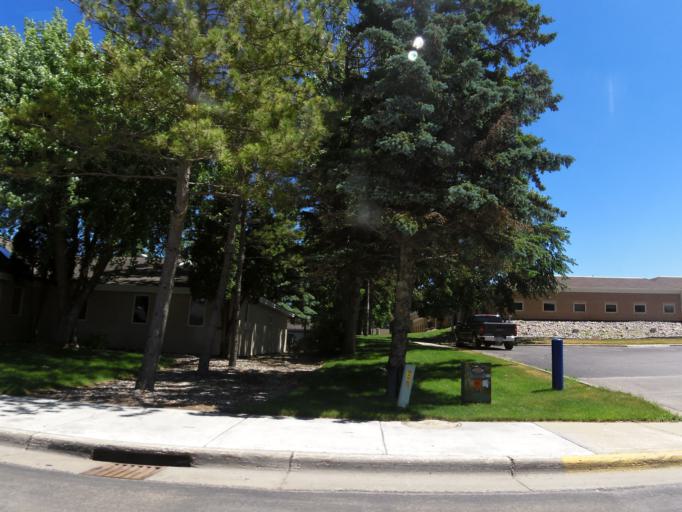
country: US
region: Minnesota
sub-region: Becker County
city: Detroit Lakes
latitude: 46.8100
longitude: -95.8457
